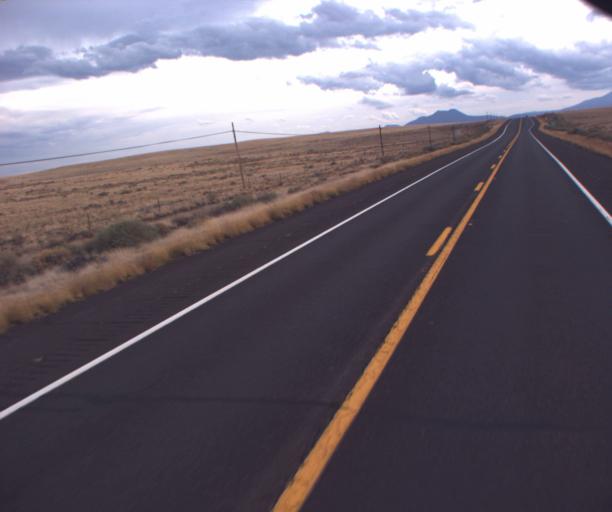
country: US
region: Arizona
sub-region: Coconino County
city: Flagstaff
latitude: 35.6390
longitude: -111.5184
